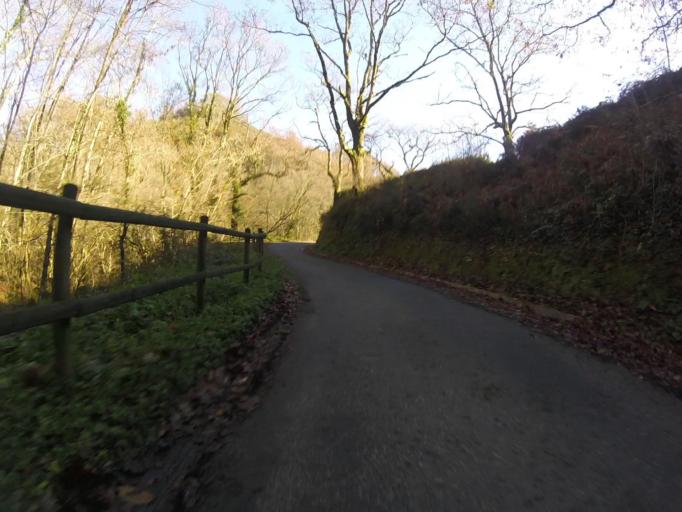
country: ES
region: Navarre
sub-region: Provincia de Navarra
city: Bera
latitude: 43.2869
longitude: -1.6426
